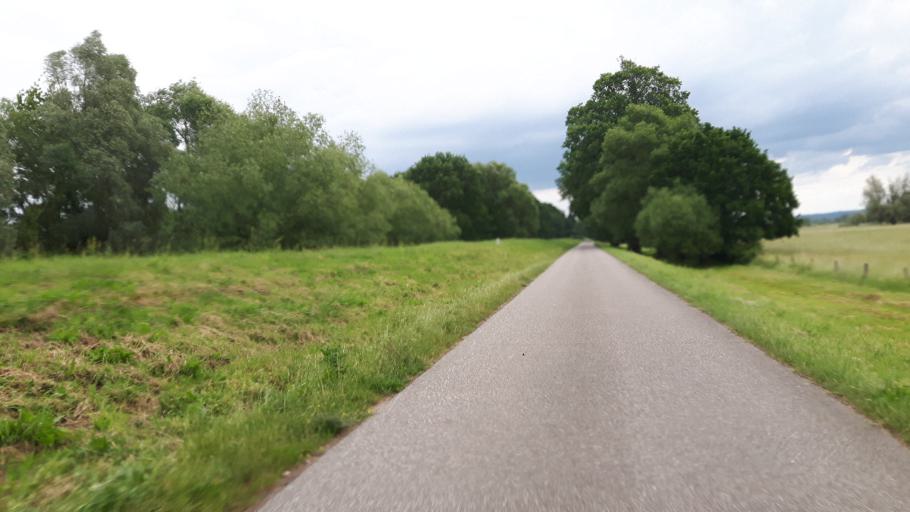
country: DE
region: Brandenburg
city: Schoneberg
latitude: 52.9839
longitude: 14.1357
